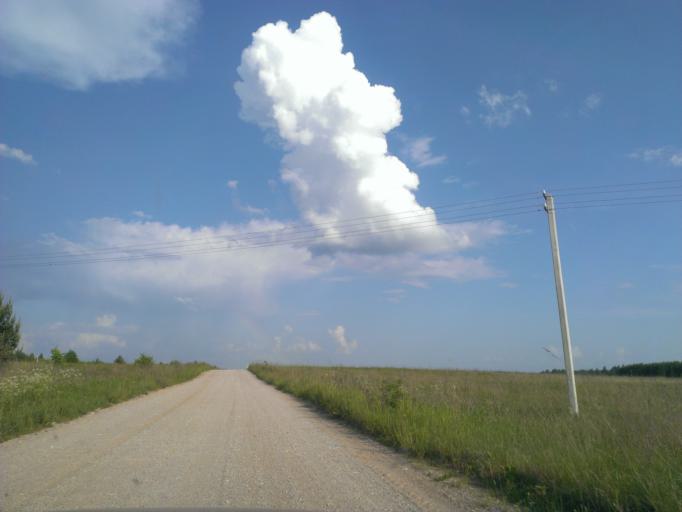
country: LT
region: Klaipedos apskritis
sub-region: Palanga
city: Sventoji
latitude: 56.0292
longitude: 21.1920
